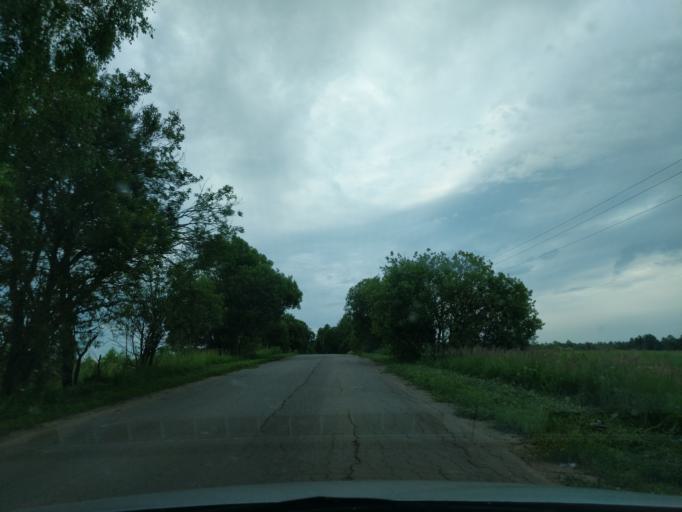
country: RU
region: Kaluga
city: Myatlevo
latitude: 54.7792
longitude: 35.7259
